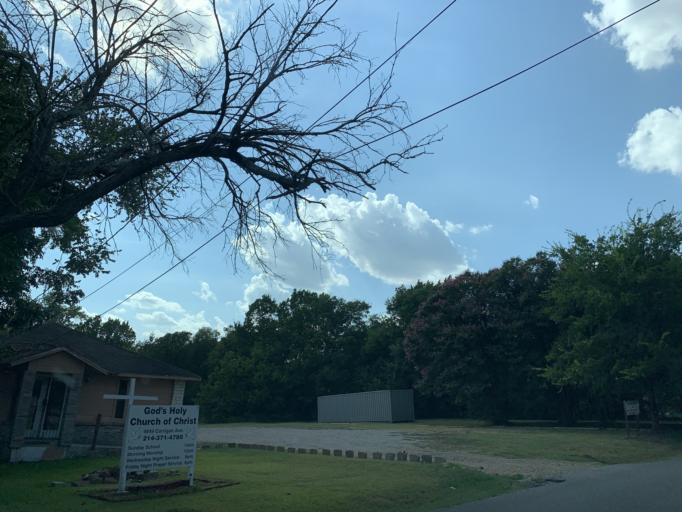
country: US
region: Texas
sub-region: Dallas County
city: Hutchins
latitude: 32.6932
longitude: -96.7776
